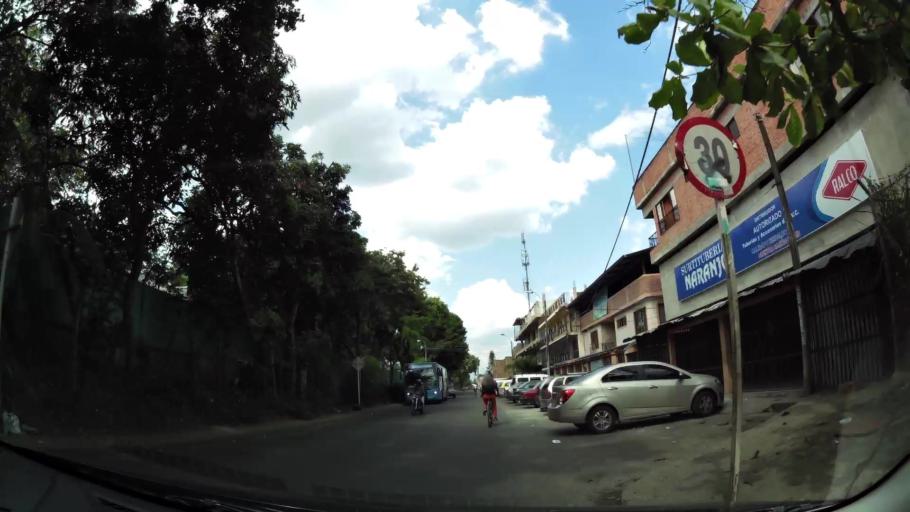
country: CO
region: Valle del Cauca
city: Cali
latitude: 3.3958
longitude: -76.5136
